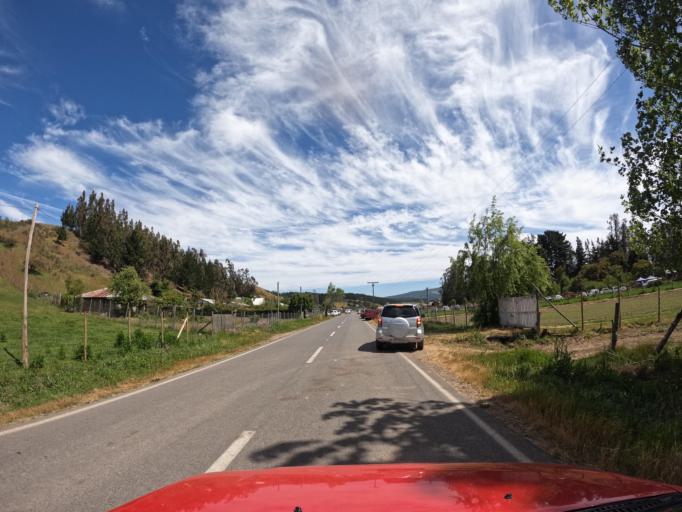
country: CL
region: Maule
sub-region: Provincia de Talca
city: Constitucion
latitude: -35.0155
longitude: -72.0379
